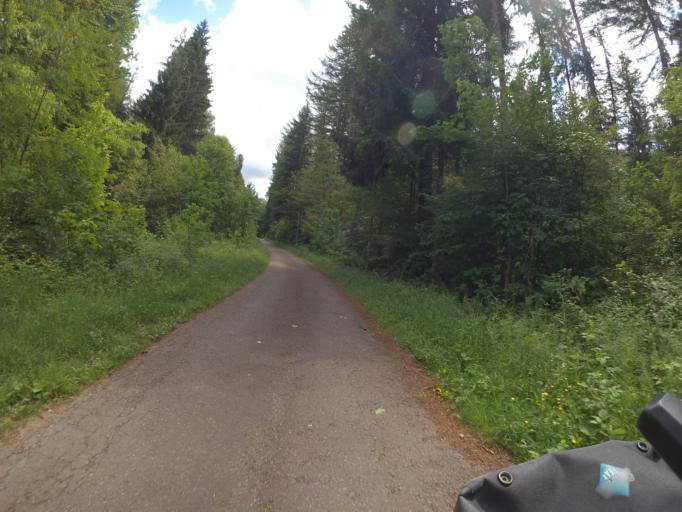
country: DE
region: Rheinland-Pfalz
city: Ludwigswinkel
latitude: 49.0868
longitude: 7.6493
